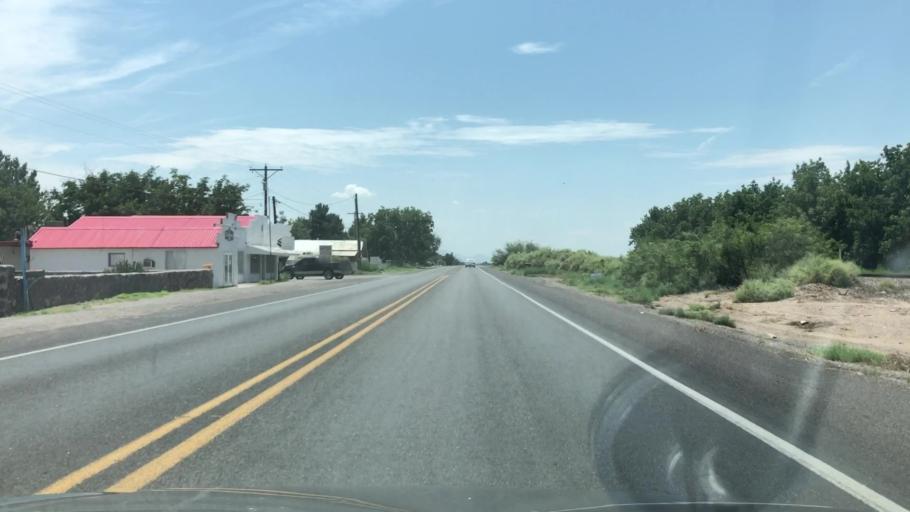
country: US
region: New Mexico
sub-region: Dona Ana County
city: Mesquite
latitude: 32.2020
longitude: -106.7203
